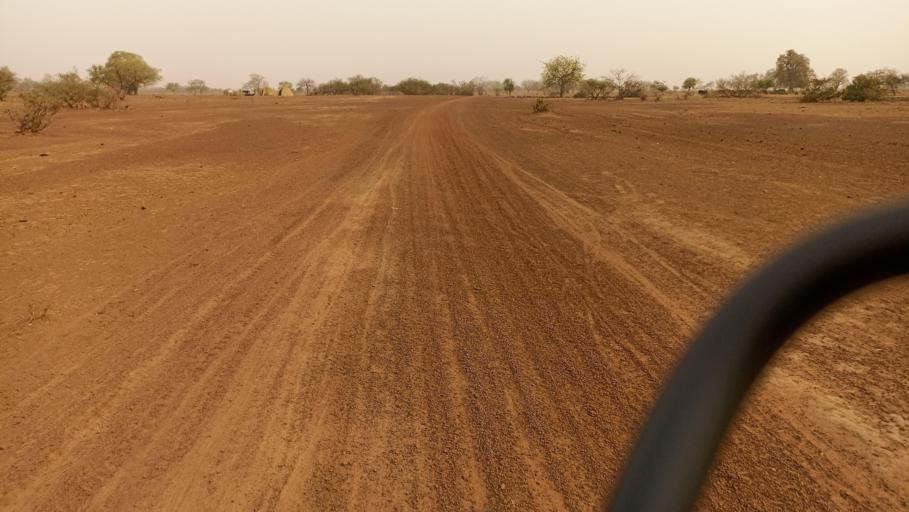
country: BF
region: Nord
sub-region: Province du Zondoma
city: Gourcy
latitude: 13.1447
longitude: -2.5974
